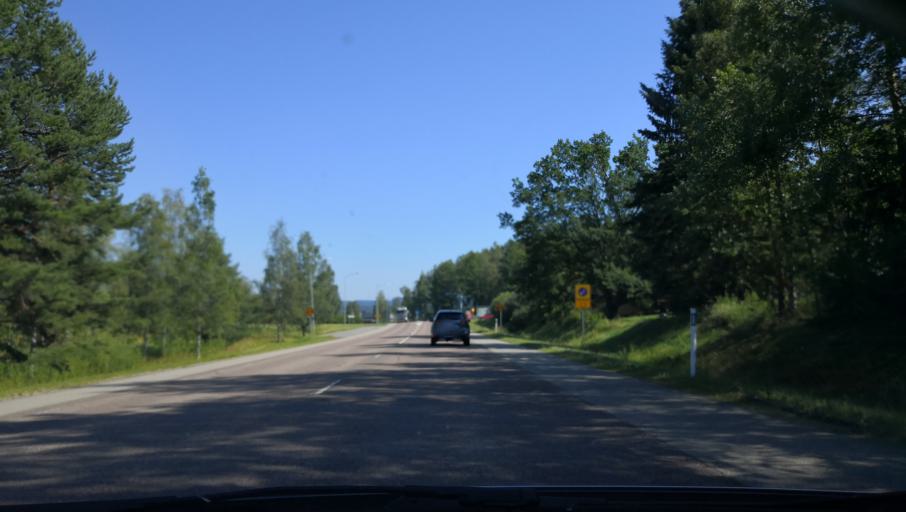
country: SE
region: Gaevleborg
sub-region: Bollnas Kommun
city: Bollnas
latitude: 61.3442
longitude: 16.3609
